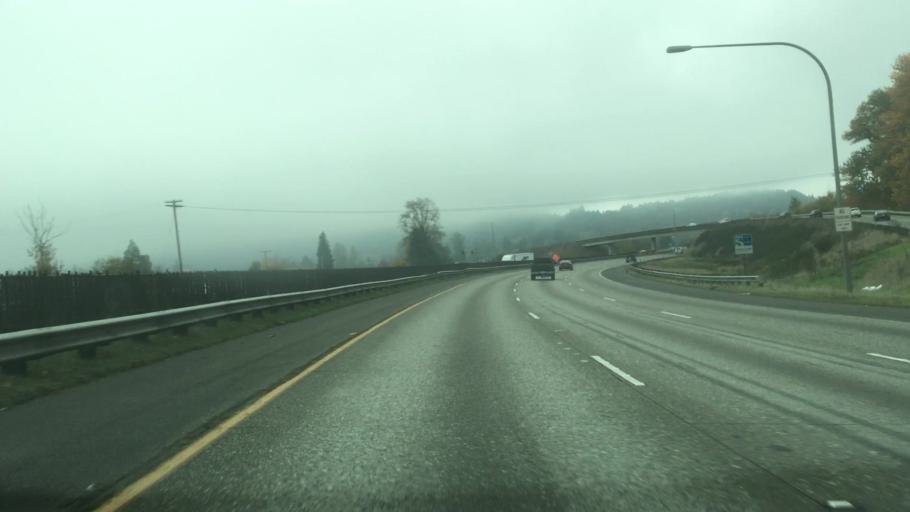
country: US
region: Washington
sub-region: Thurston County
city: Tanglewilde-Thompson Place
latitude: 47.0687
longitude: -122.7123
